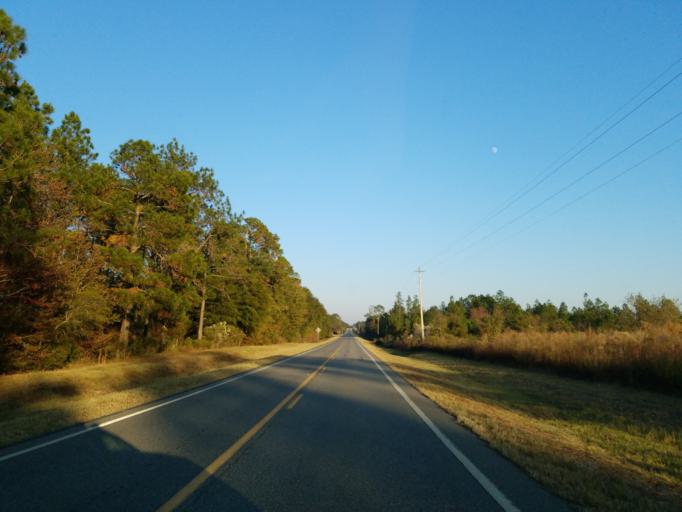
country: US
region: Georgia
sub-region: Turner County
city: Ashburn
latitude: 31.8596
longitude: -83.6436
